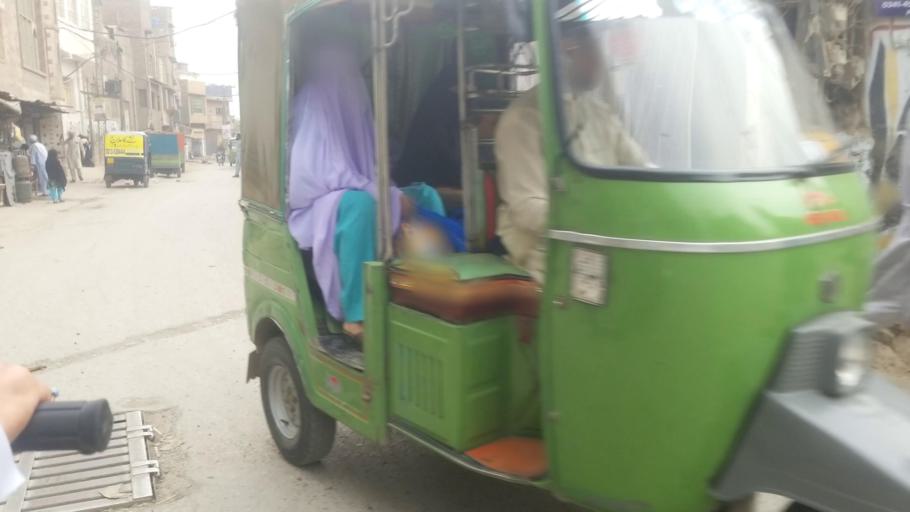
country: PK
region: Khyber Pakhtunkhwa
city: Peshawar
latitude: 33.9933
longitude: 71.5565
